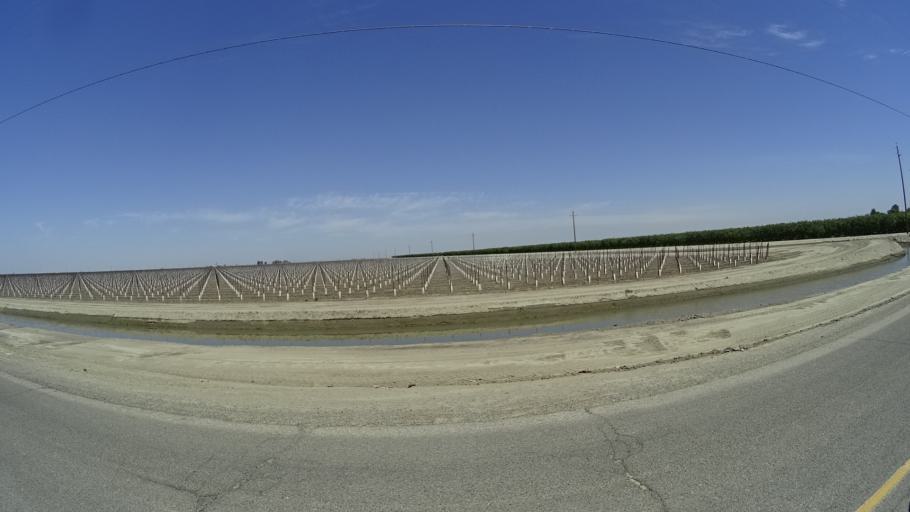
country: US
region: California
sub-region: Kings County
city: Corcoran
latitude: 36.1161
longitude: -119.6338
